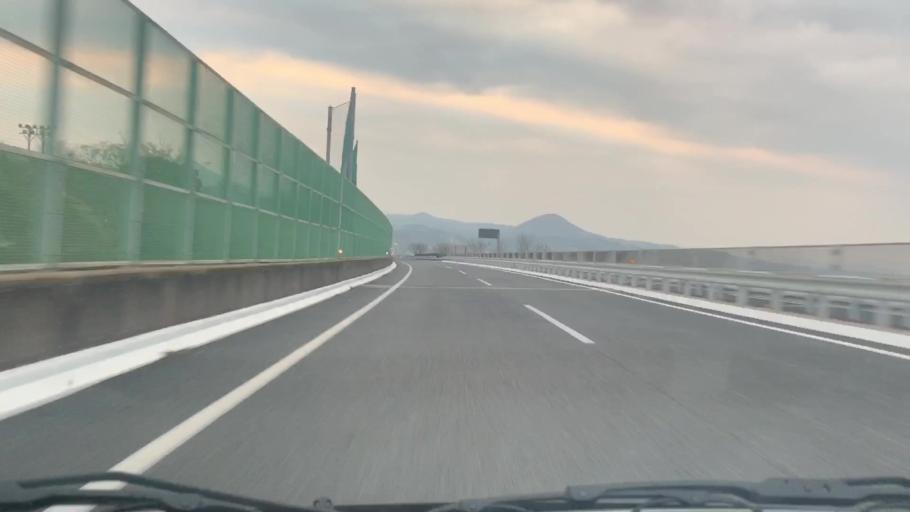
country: JP
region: Saga Prefecture
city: Ureshinomachi-shimojuku
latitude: 33.0306
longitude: 129.9295
